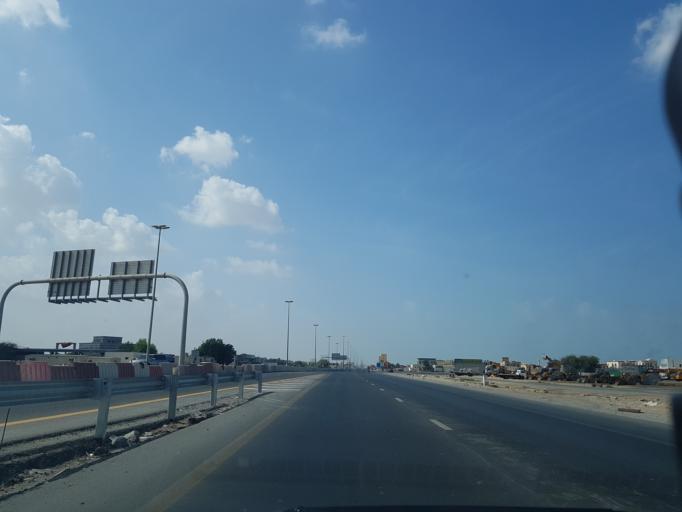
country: AE
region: Ra's al Khaymah
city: Ras al-Khaimah
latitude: 25.8333
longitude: 56.0123
